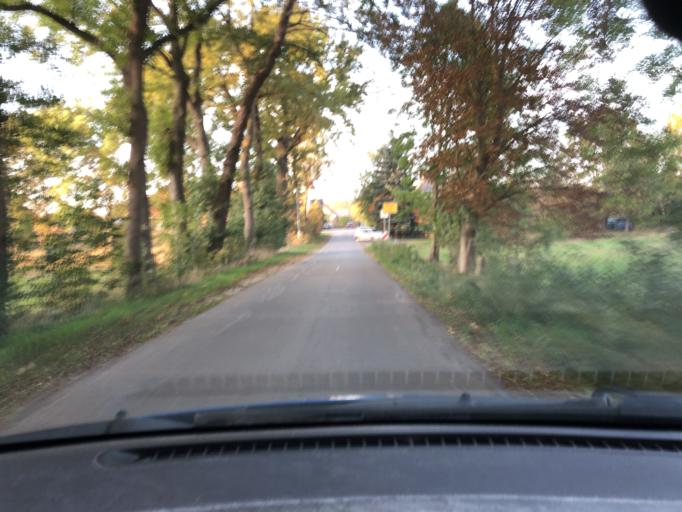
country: DE
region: Lower Saxony
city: Hitzacker
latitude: 53.1495
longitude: 11.0042
